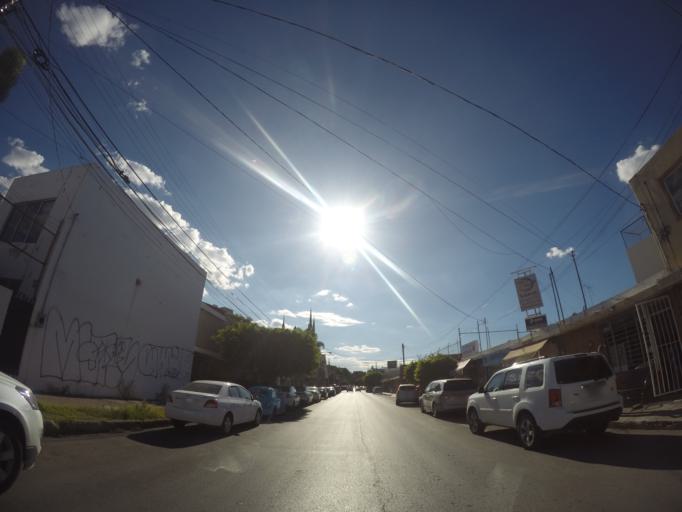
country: MX
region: San Luis Potosi
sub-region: San Luis Potosi
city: San Luis Potosi
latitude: 22.1476
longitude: -101.0026
